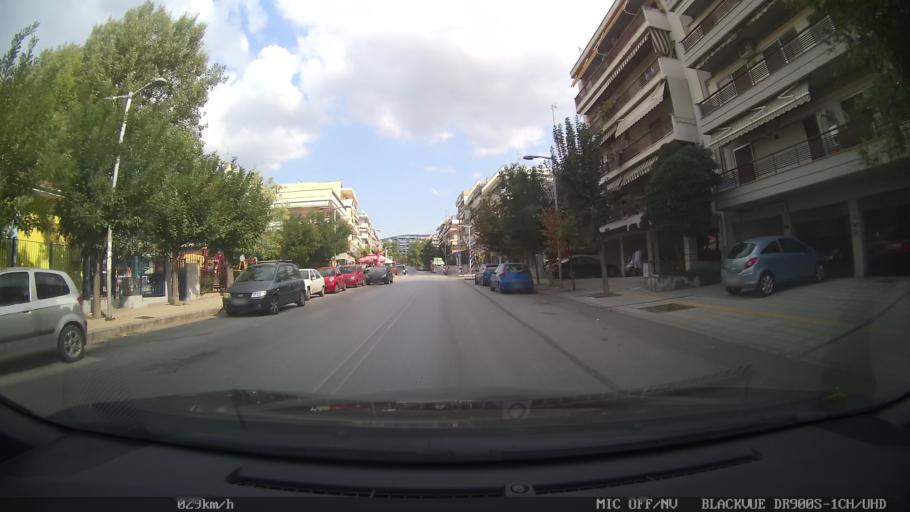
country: GR
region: Central Macedonia
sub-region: Nomos Thessalonikis
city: Triandria
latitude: 40.6094
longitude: 22.9842
